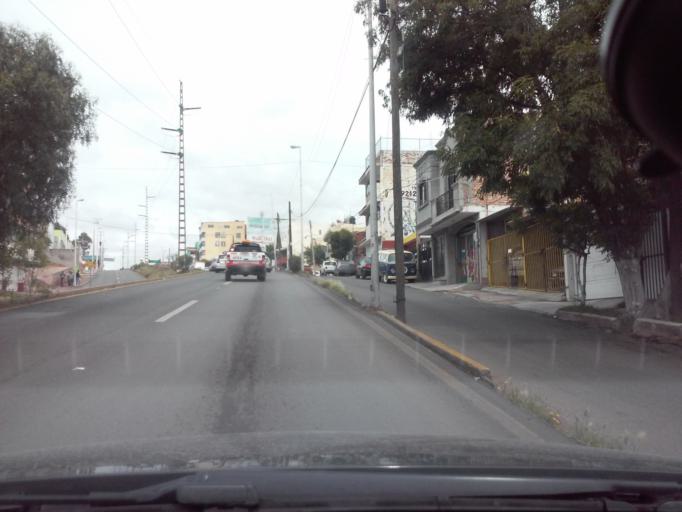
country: MX
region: Zacatecas
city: Zacatecas
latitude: 22.7609
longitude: -102.5761
